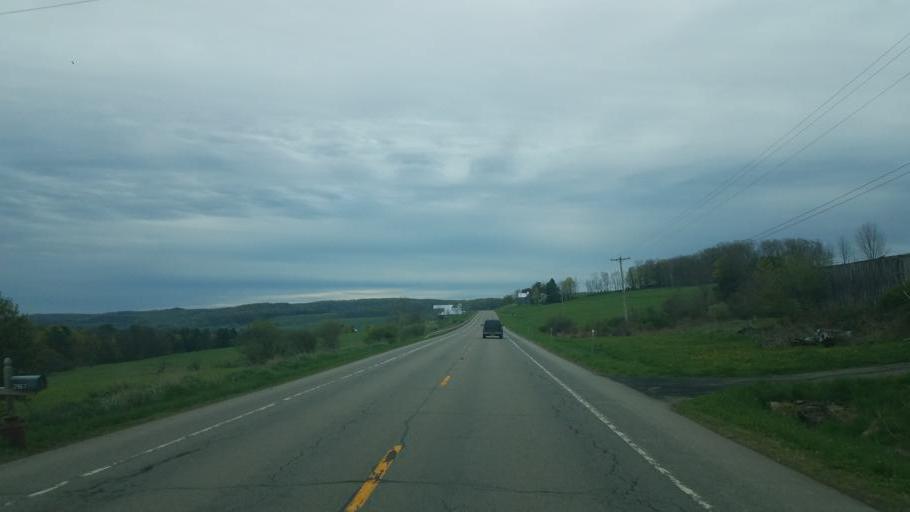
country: US
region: New York
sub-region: Steuben County
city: Canisteo
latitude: 42.1444
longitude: -77.5174
